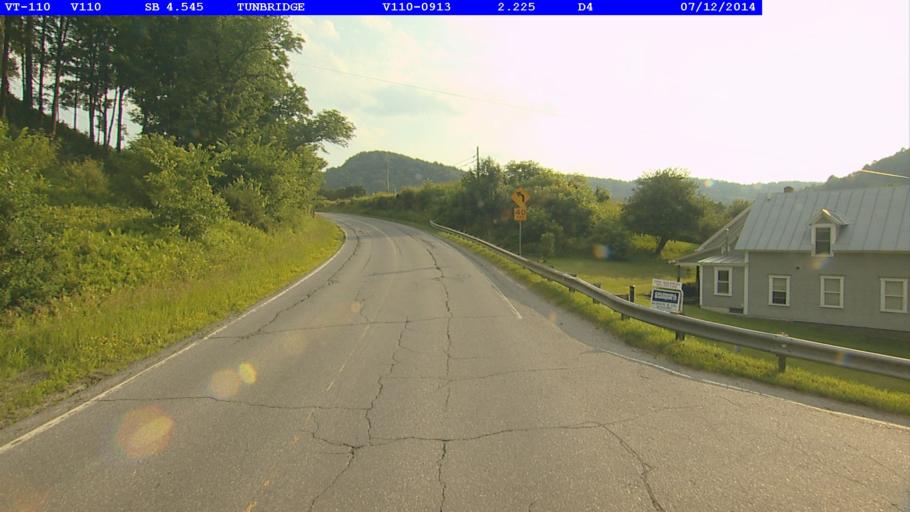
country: US
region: Vermont
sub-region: Orange County
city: Chelsea
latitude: 43.8820
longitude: -72.5007
